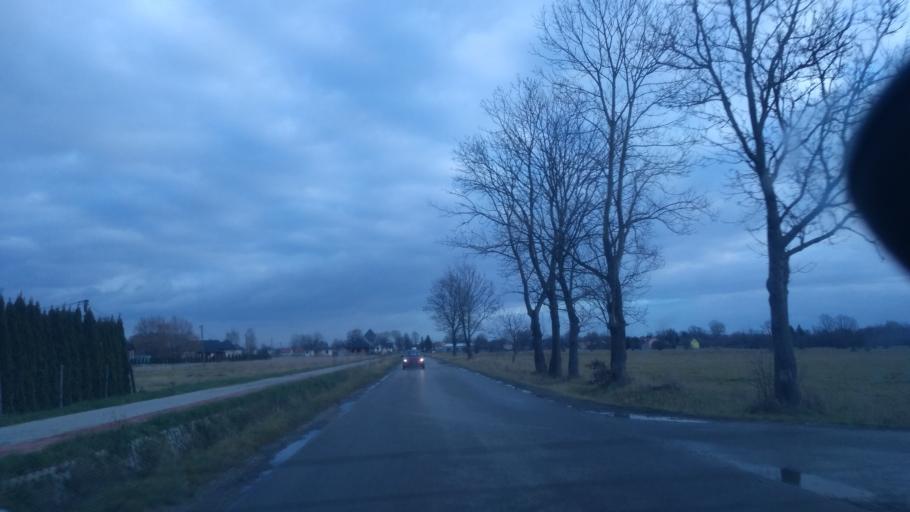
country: PL
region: Subcarpathian Voivodeship
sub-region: Powiat lancucki
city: Czarna
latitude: 50.0936
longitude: 22.1706
